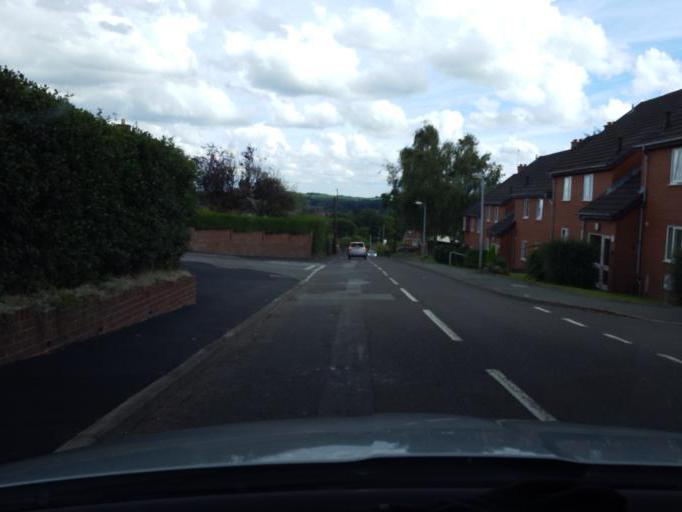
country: GB
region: Wales
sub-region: Wrexham
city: Rhosllanerchrugog
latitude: 52.9752
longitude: -3.0888
